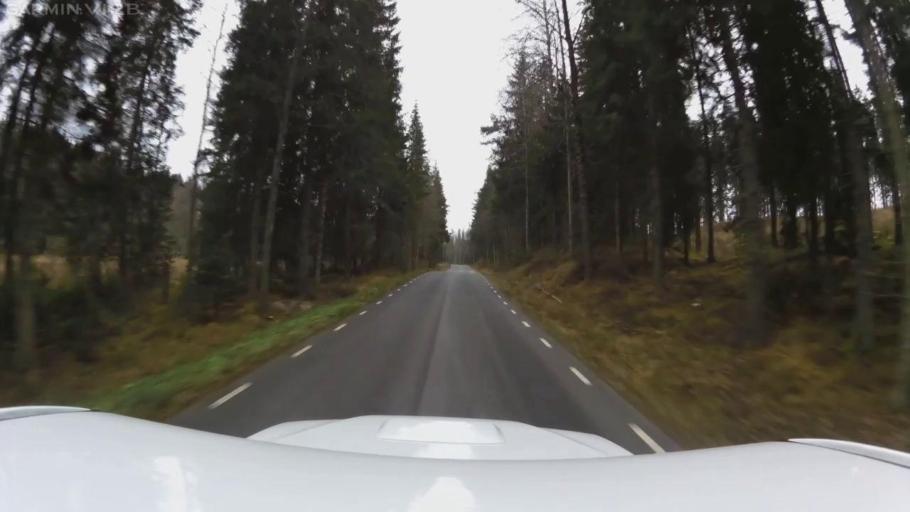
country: SE
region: OEstergoetland
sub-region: Mjolby Kommun
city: Mantorp
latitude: 58.1682
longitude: 15.3974
